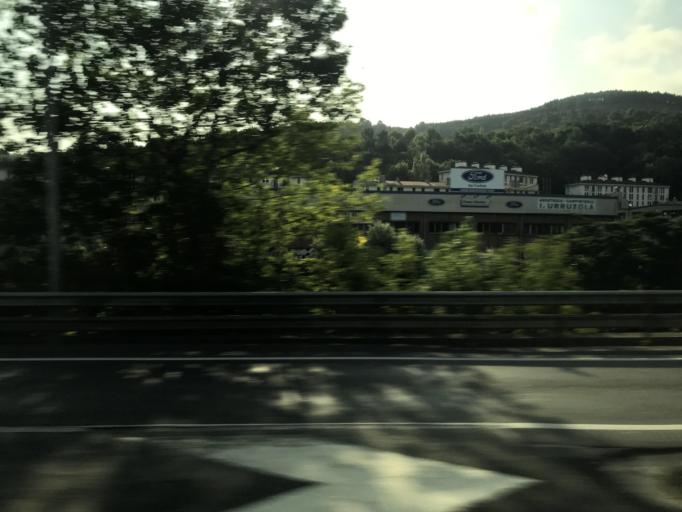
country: ES
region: Basque Country
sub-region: Provincia de Guipuzcoa
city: Oria
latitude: 43.2548
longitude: -2.0210
